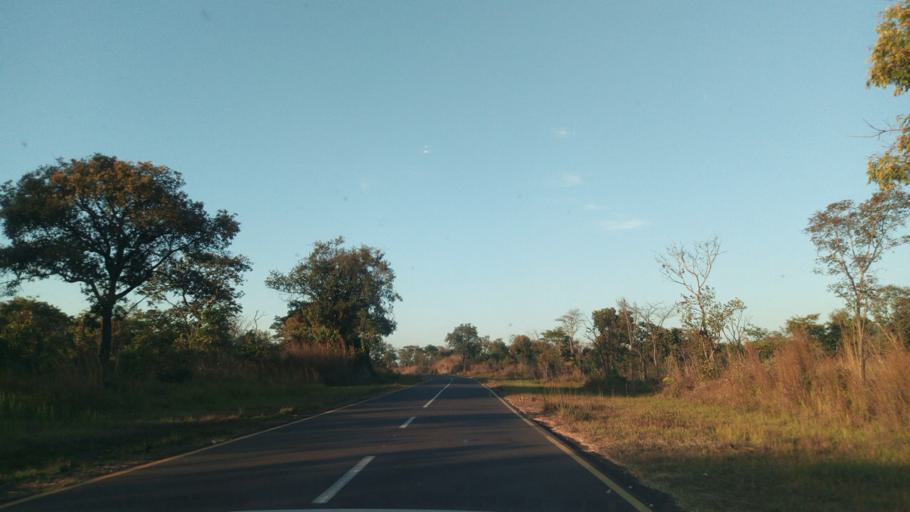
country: ZM
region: Luapula
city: Mwense
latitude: -10.7781
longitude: 28.2476
